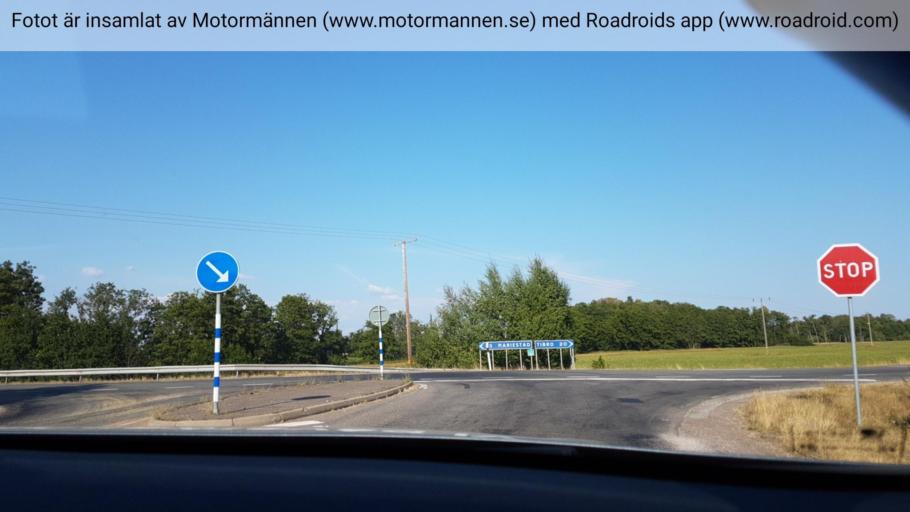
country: SE
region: Vaestra Goetaland
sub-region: Toreboda Kommun
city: Toereboda
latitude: 58.5752
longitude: 14.0964
